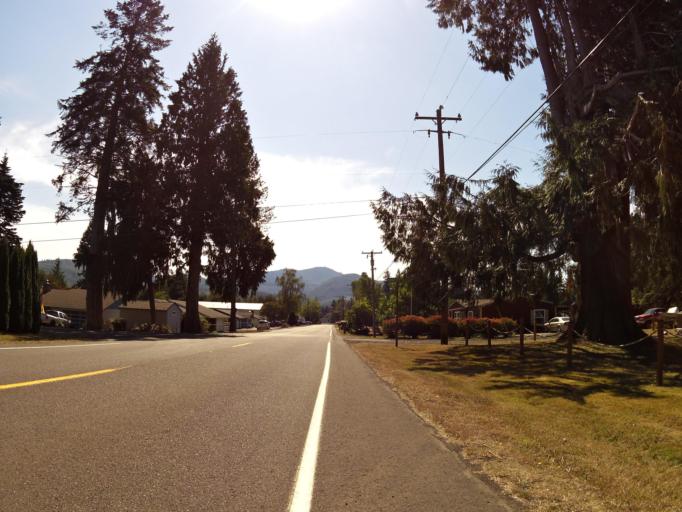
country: US
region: Washington
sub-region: Wahkiakum County
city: Cathlamet
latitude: 46.1734
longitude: -123.5834
